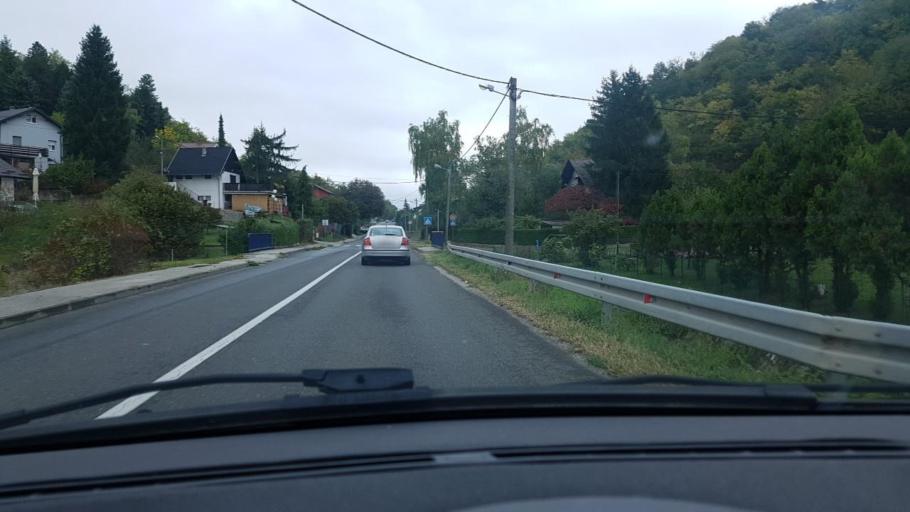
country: HR
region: Grad Zagreb
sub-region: Sesvete
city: Sesvete
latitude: 45.8871
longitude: 16.1169
